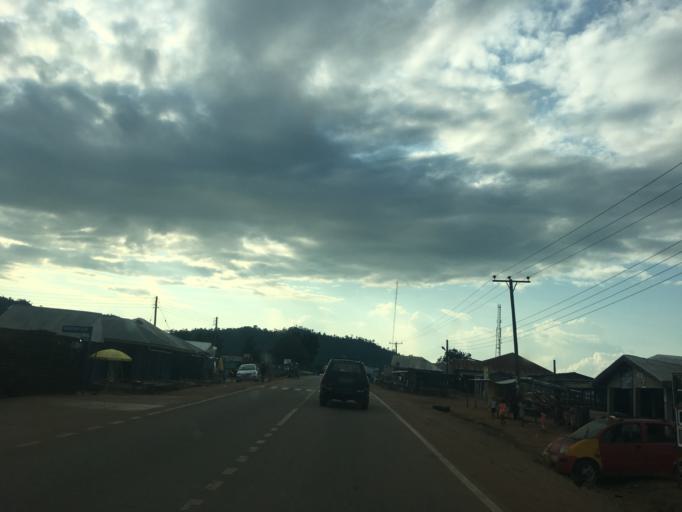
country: GH
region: Western
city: Bibiani
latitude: 6.4396
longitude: -2.3101
